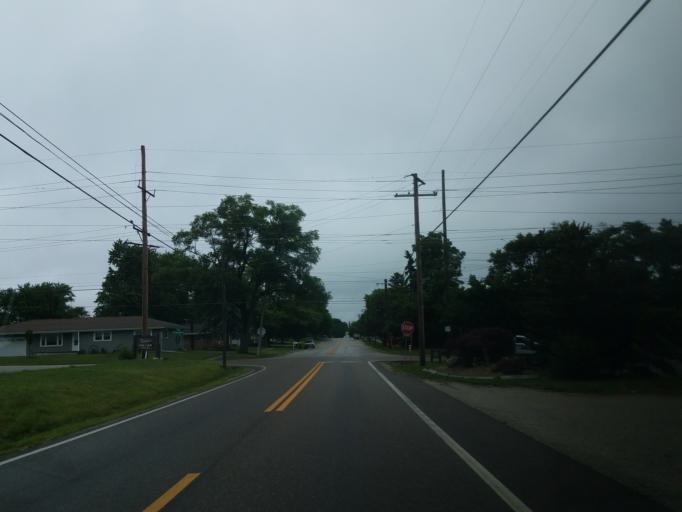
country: US
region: Illinois
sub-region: McLean County
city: Bloomington
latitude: 40.4631
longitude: -88.9817
